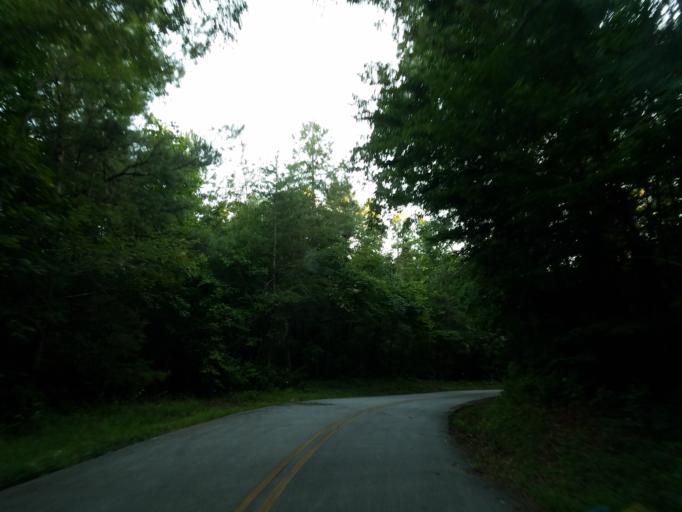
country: US
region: Georgia
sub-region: Lumpkin County
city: Dahlonega
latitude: 34.4220
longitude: -83.9936
